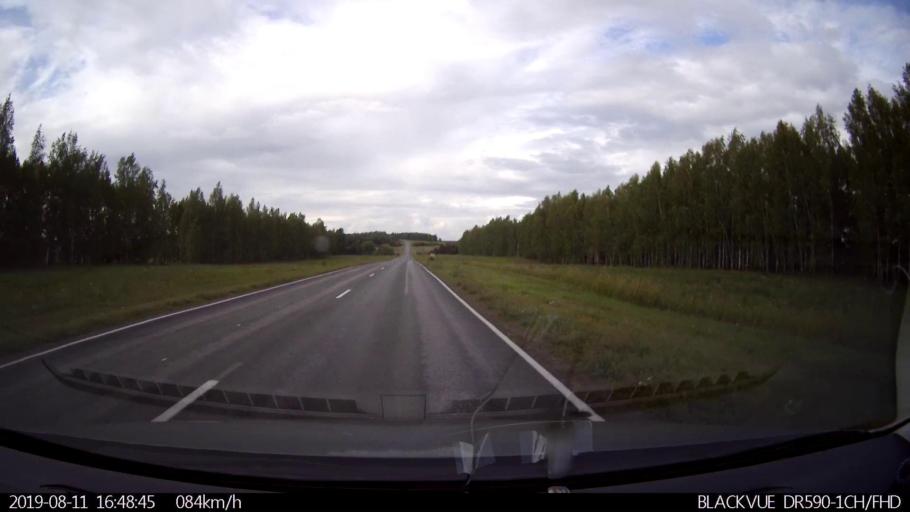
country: RU
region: Ulyanovsk
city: Mayna
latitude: 54.2126
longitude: 47.6933
